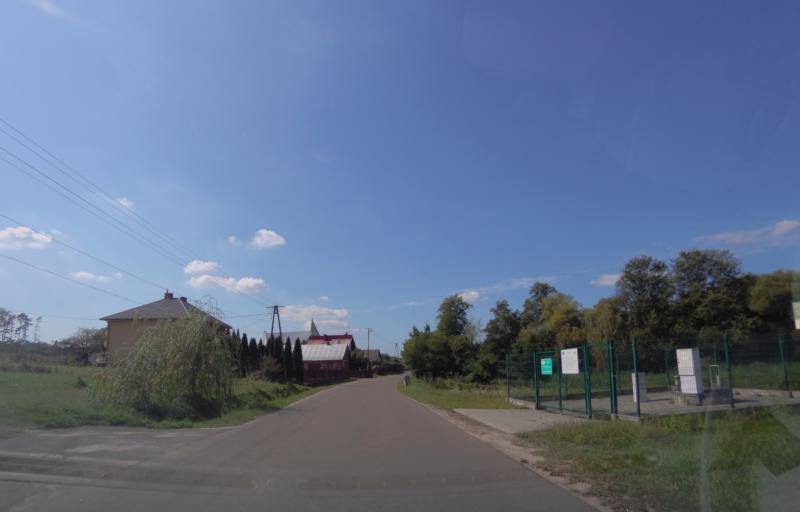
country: PL
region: Subcarpathian Voivodeship
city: Nowa Sarzyna
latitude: 50.3054
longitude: 22.3249
